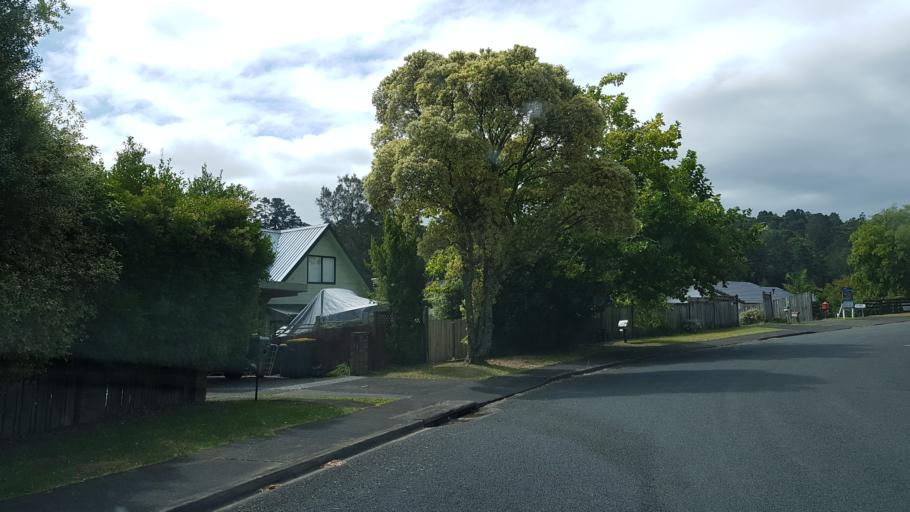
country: NZ
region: Auckland
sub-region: Auckland
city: North Shore
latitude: -36.7749
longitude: 174.7009
